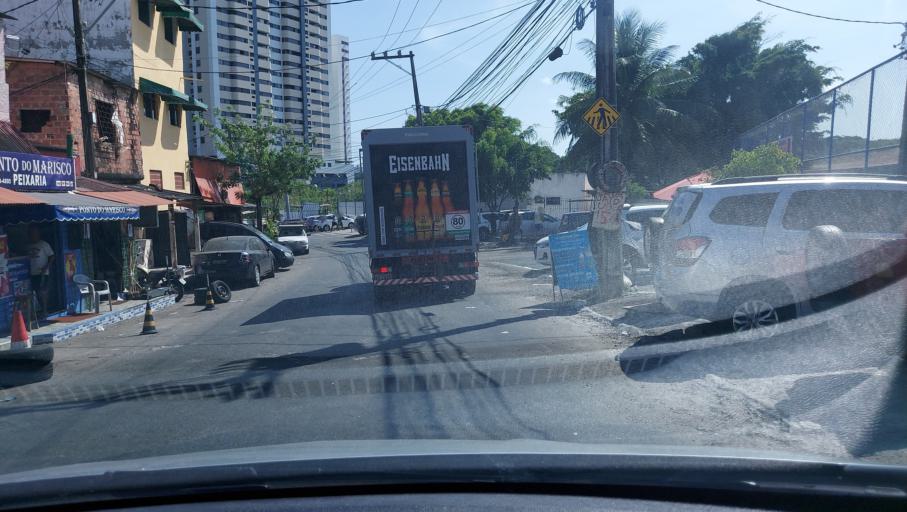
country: BR
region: Bahia
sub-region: Salvador
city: Salvador
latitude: -12.9771
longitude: -38.4416
